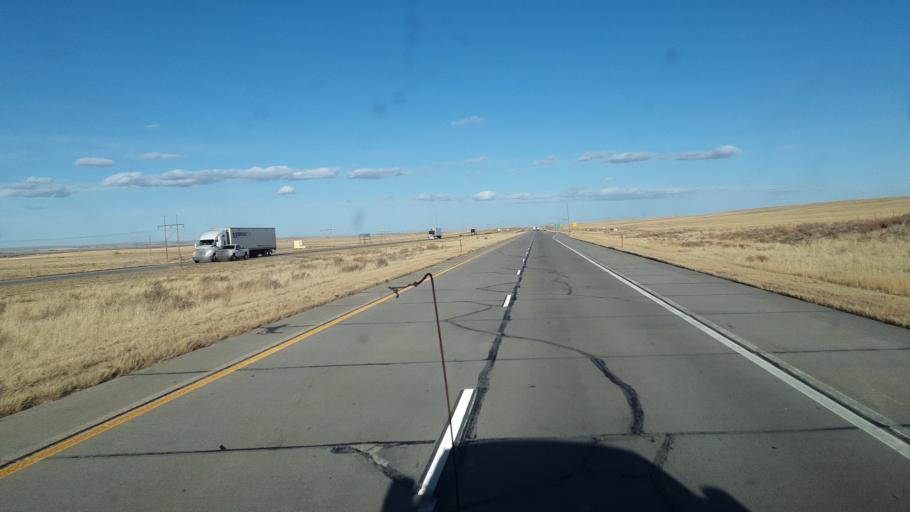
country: US
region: Colorado
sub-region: Logan County
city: Sterling
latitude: 40.7048
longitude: -103.0616
